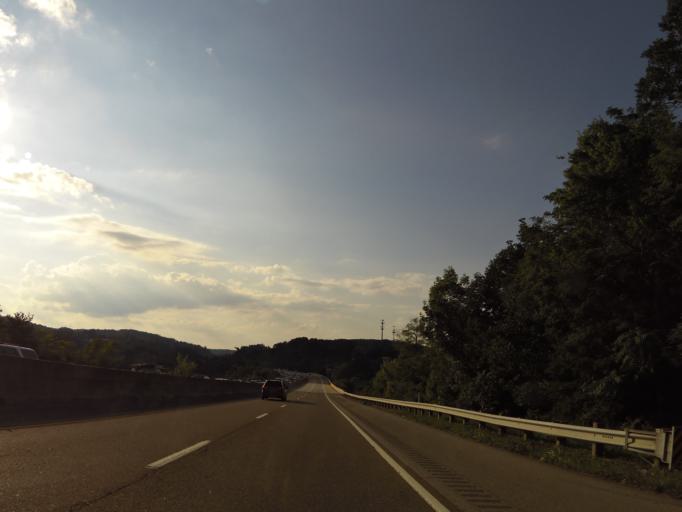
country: US
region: Tennessee
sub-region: Knox County
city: Farragut
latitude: 35.8822
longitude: -84.0996
